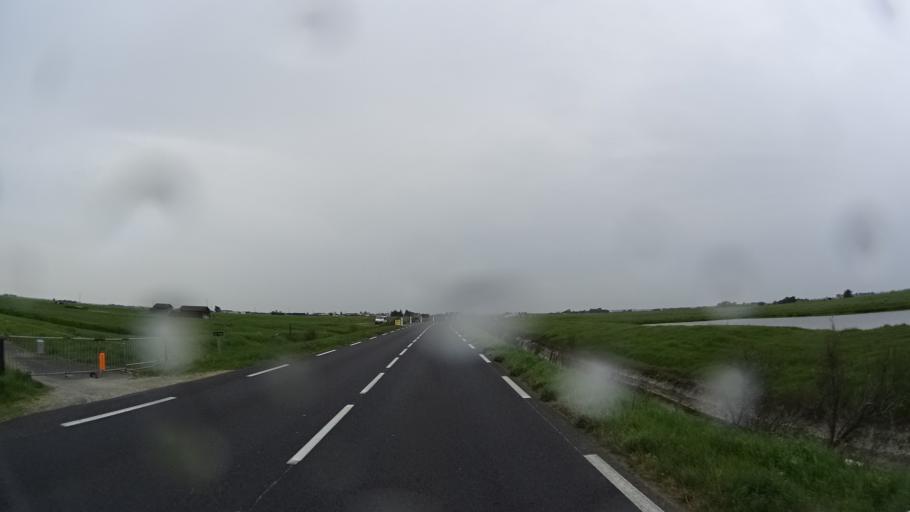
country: FR
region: Pays de la Loire
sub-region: Departement de la Vendee
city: Beauvoir-sur-Mer
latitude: 46.9027
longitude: -2.0585
